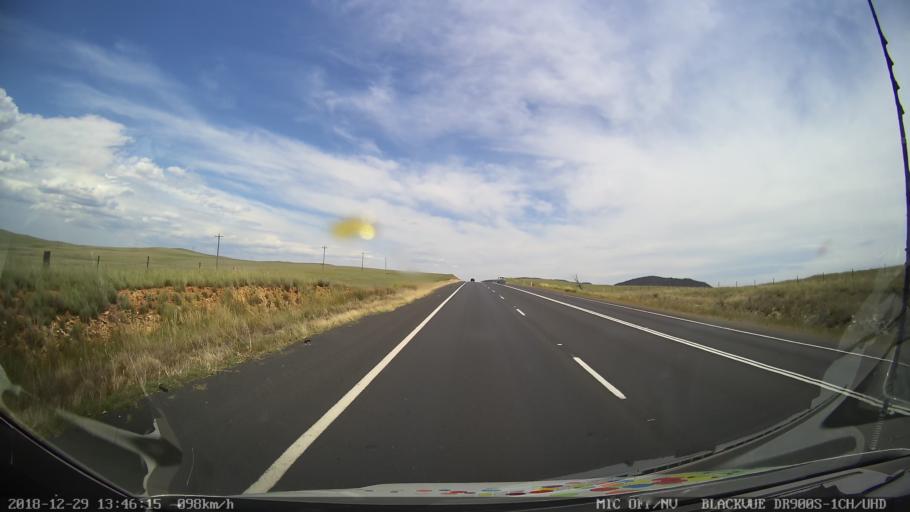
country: AU
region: New South Wales
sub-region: Cooma-Monaro
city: Cooma
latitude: -36.1090
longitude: 149.1433
